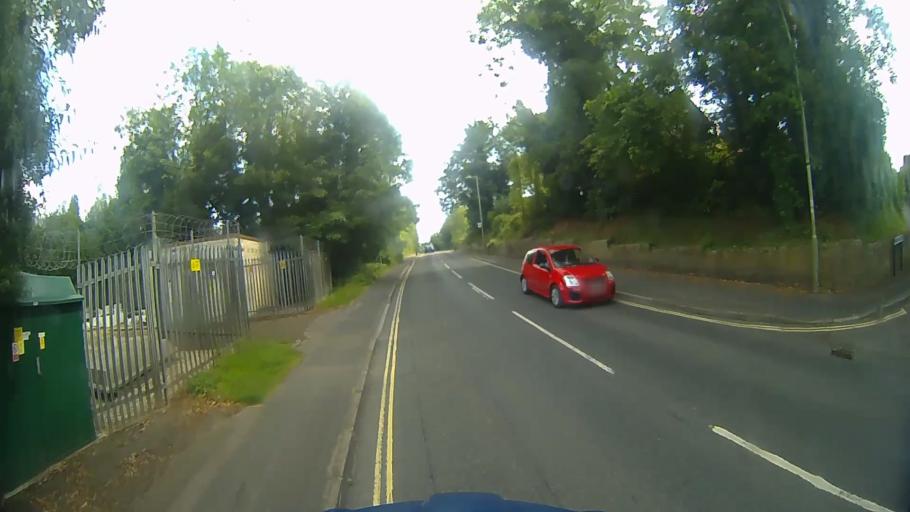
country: GB
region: England
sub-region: Hampshire
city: Andover
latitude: 51.2173
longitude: -1.4968
